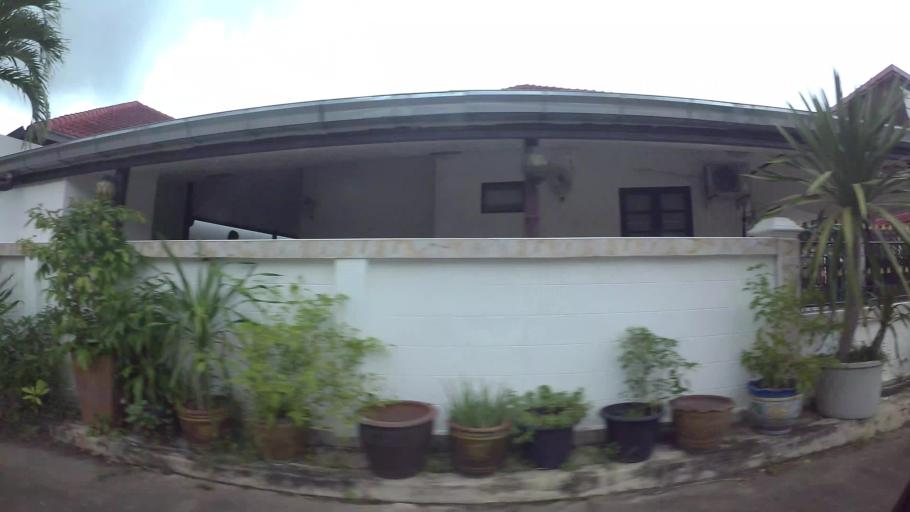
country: TH
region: Chon Buri
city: Sattahip
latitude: 12.7274
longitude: 100.8974
